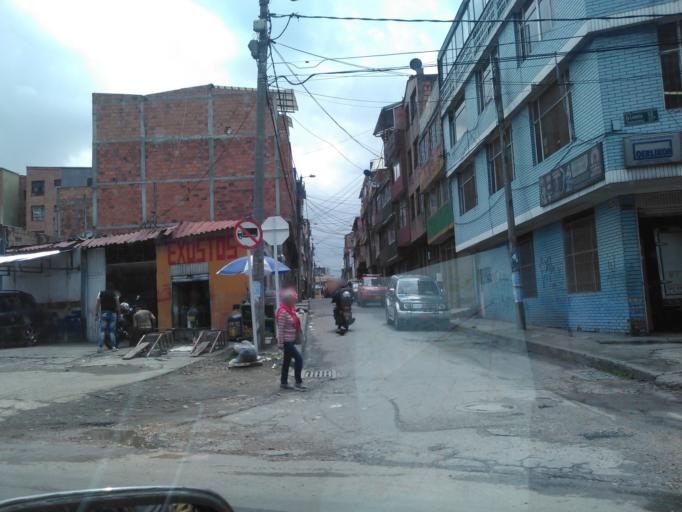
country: CO
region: Bogota D.C.
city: Bogota
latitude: 4.6217
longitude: -74.1250
